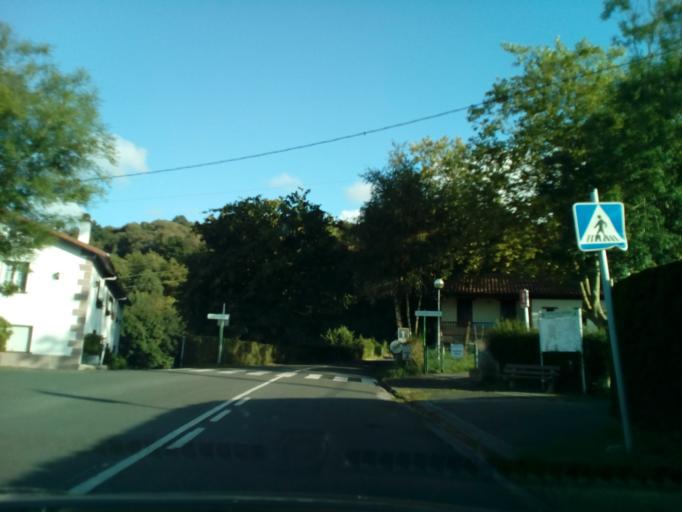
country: ES
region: Basque Country
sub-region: Provincia de Guipuzcoa
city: Urnieta
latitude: 43.2268
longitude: -1.9860
